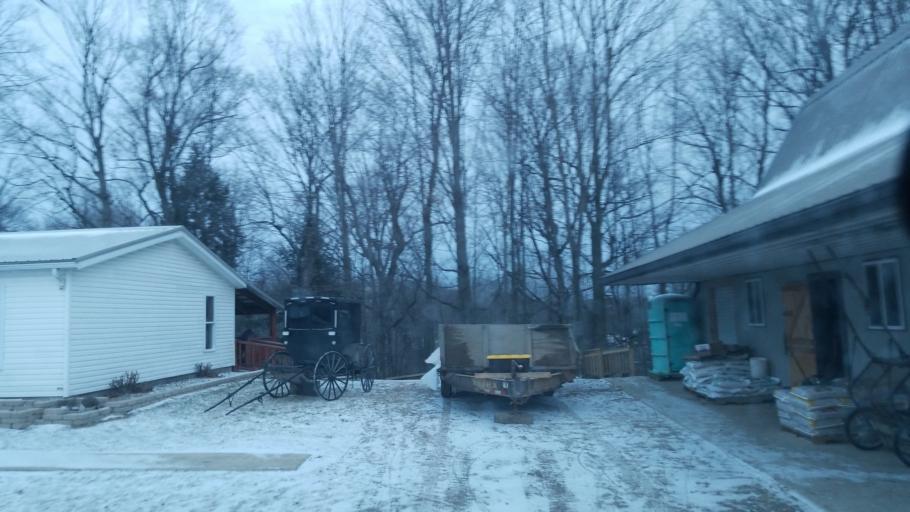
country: US
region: Michigan
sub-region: Osceola County
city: Reed City
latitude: 43.8299
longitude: -85.4313
